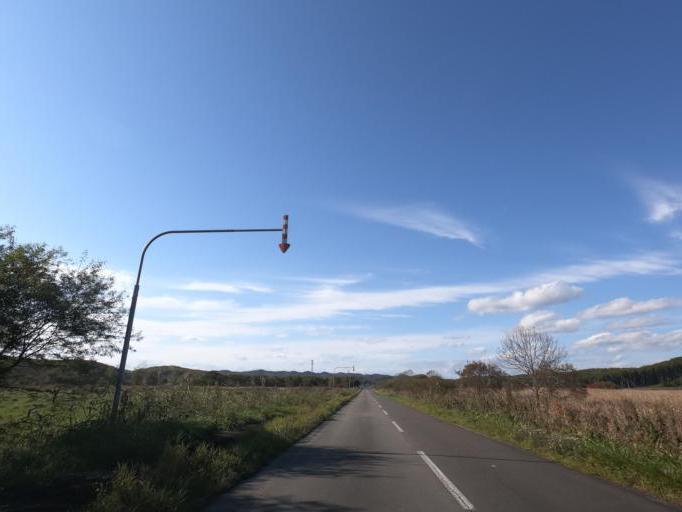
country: JP
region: Hokkaido
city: Obihiro
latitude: 42.6387
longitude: 143.5119
